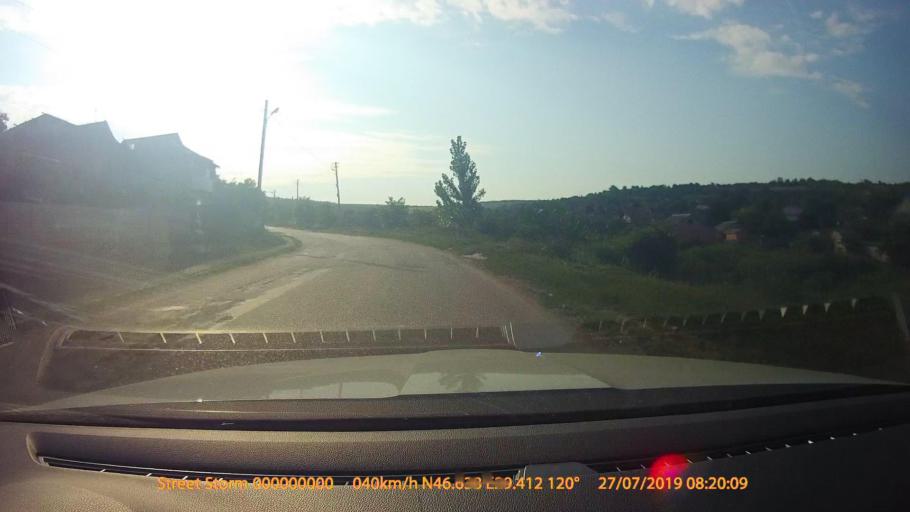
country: MD
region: Causeni
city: Causeni
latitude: 46.6381
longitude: 29.4122
